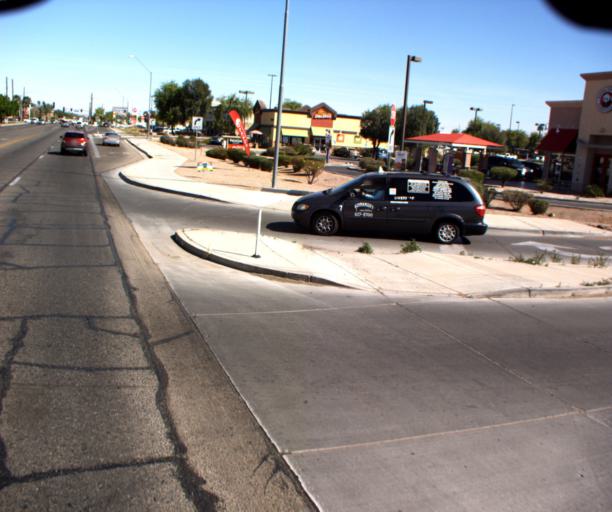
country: US
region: Arizona
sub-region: Yuma County
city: Yuma
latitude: 32.6817
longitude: -114.6503
